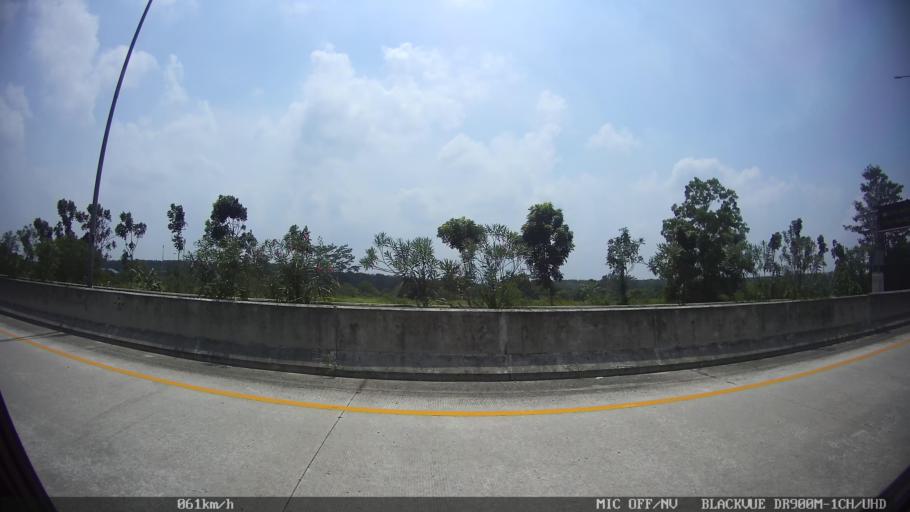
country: ID
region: Lampung
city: Kedaton
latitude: -5.3614
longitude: 105.3254
